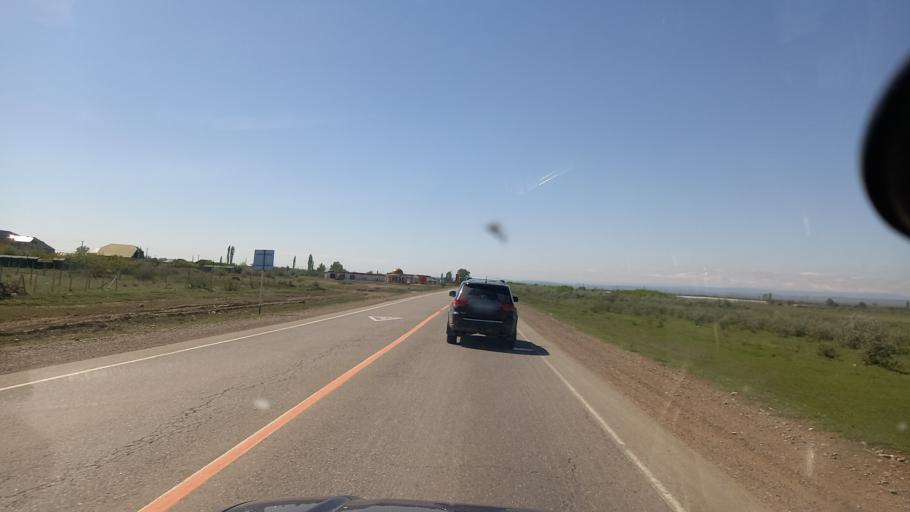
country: RU
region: Dagestan
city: Khazar
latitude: 41.9320
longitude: 48.3274
